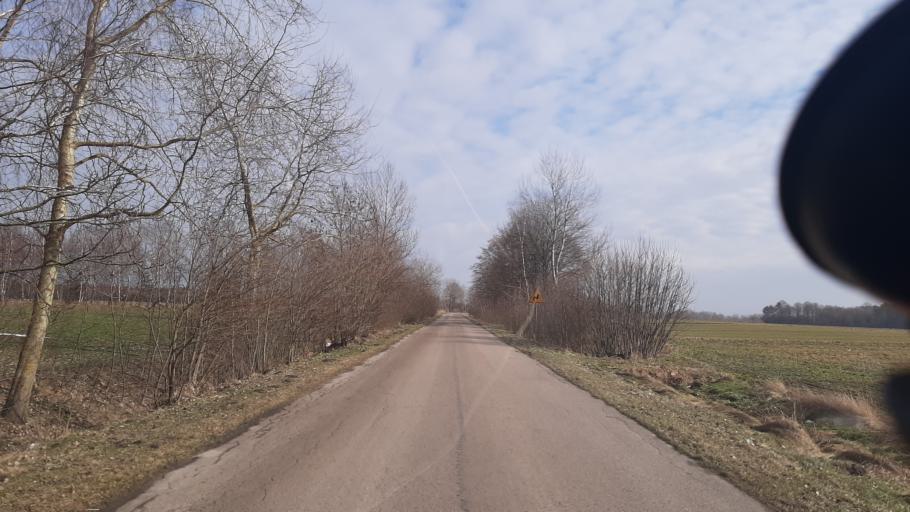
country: PL
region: Lublin Voivodeship
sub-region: Powiat lubartowski
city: Uscimow Stary
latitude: 51.4687
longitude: 22.9813
